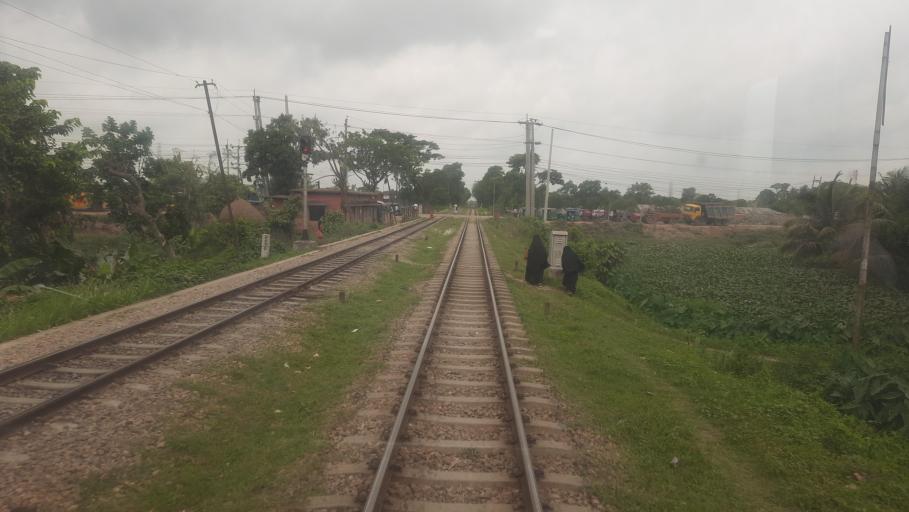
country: BD
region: Dhaka
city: Bhairab Bazar
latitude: 23.9658
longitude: 91.1023
